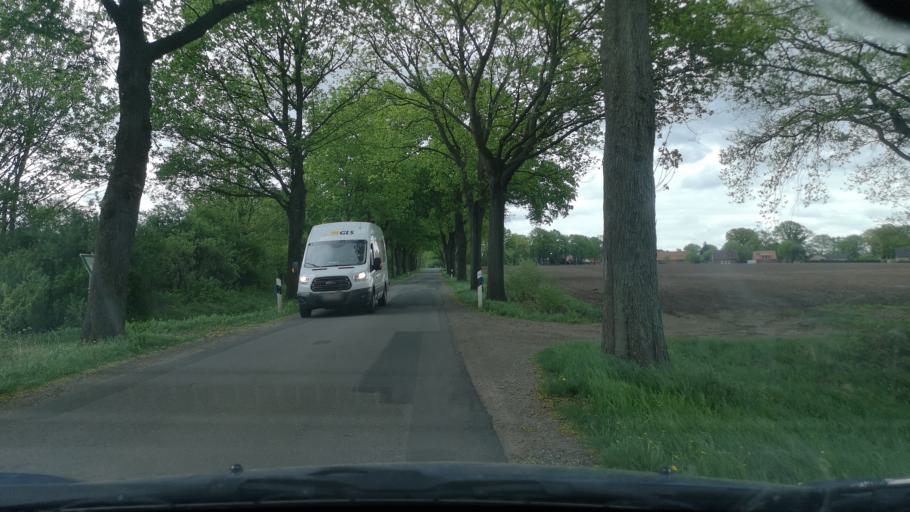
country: DE
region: Lower Saxony
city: Langenhagen
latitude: 52.4870
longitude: 9.7592
